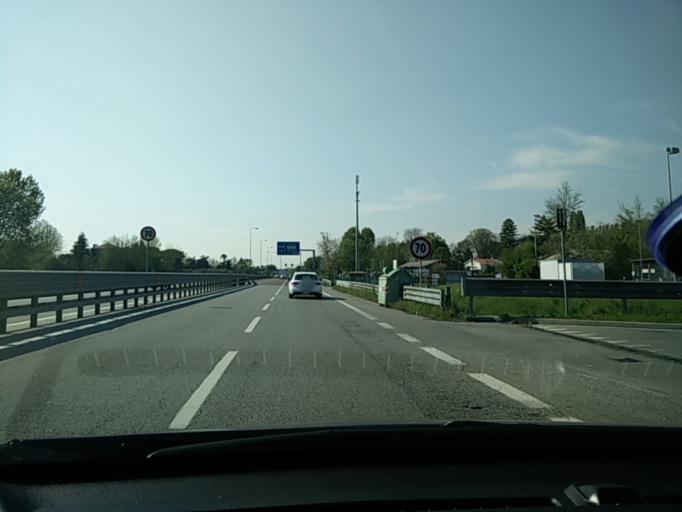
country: IT
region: Veneto
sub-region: Provincia di Venezia
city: Campalto
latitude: 45.5088
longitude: 12.2662
